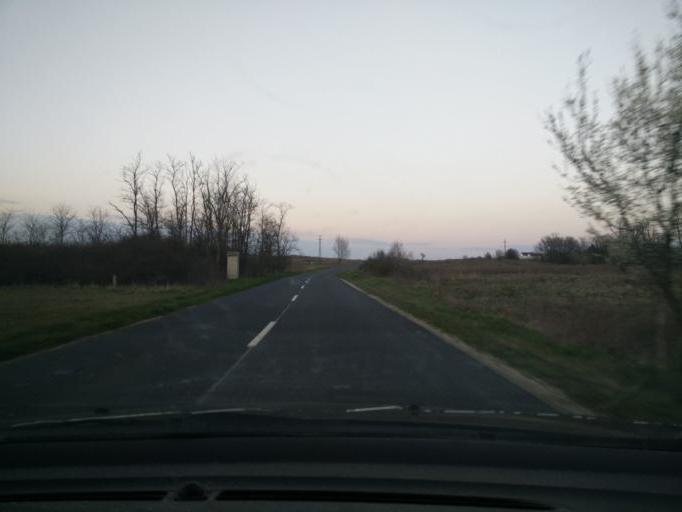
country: HU
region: Veszprem
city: Csabrendek
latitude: 47.0352
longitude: 17.3087
